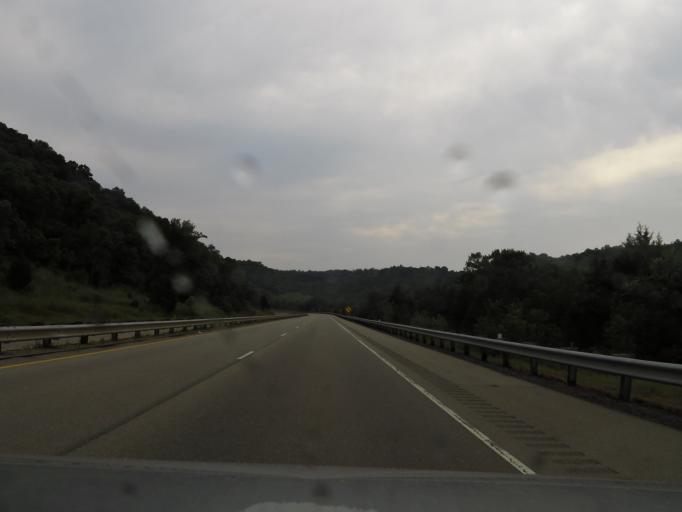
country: US
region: Ohio
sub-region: Brown County
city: Ripley
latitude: 38.7611
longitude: -83.8242
